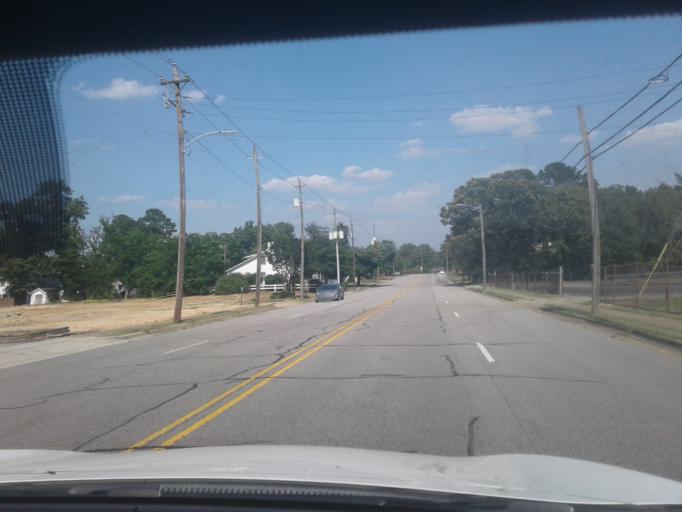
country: US
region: North Carolina
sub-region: Harnett County
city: Erwin
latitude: 35.3269
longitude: -78.6703
